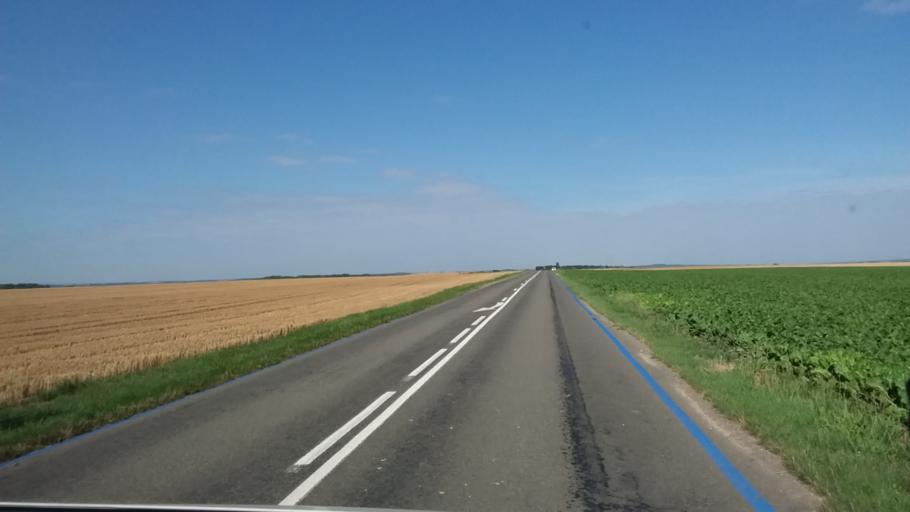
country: FR
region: Picardie
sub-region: Departement de l'Aisne
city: Bruyeres-et-Montberault
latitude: 49.4404
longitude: 3.7050
